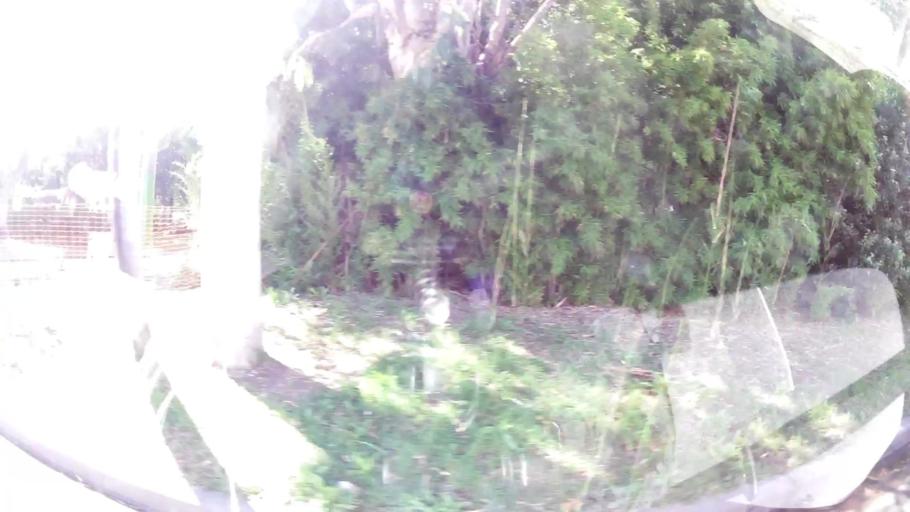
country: AR
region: Buenos Aires
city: Ituzaingo
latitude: -34.6208
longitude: -58.6559
